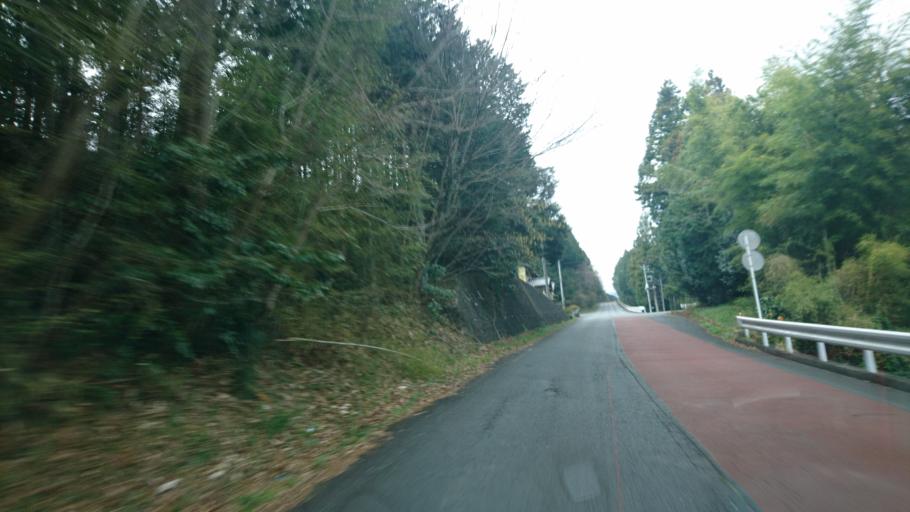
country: JP
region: Shizuoka
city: Fujinomiya
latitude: 35.2974
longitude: 138.5783
